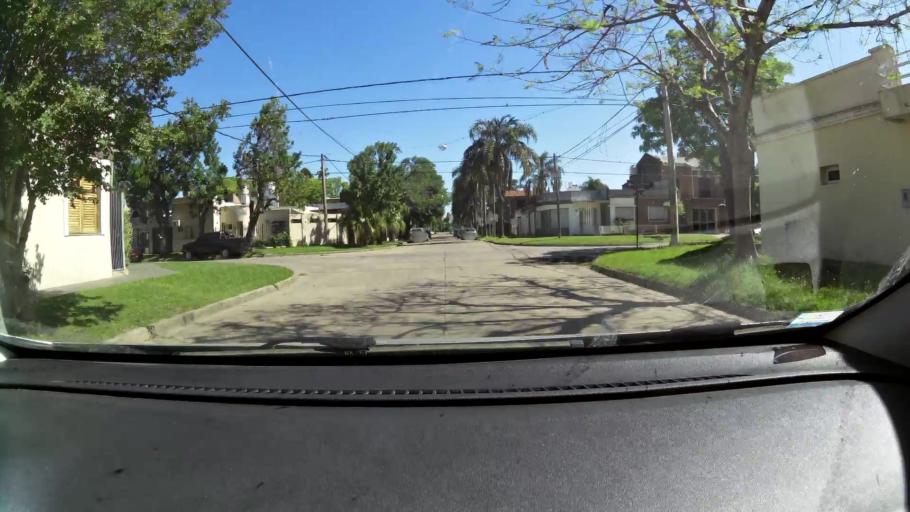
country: AR
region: Santa Fe
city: Santa Fe de la Vera Cruz
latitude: -31.6017
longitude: -60.6717
